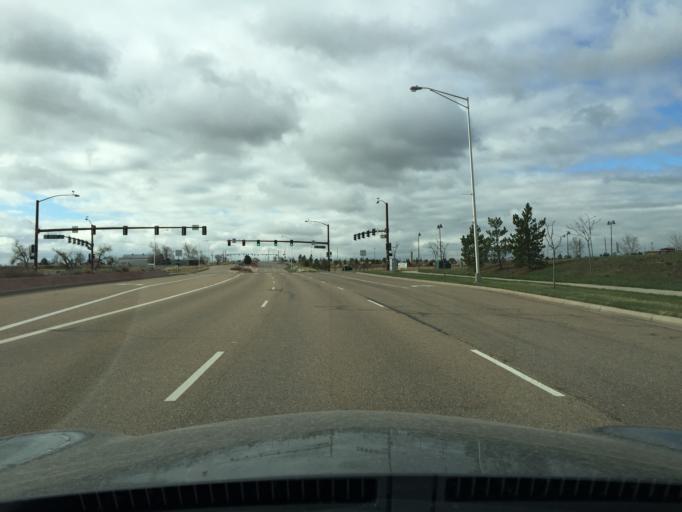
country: US
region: Colorado
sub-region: Boulder County
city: Erie
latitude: 39.9947
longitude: -104.9784
